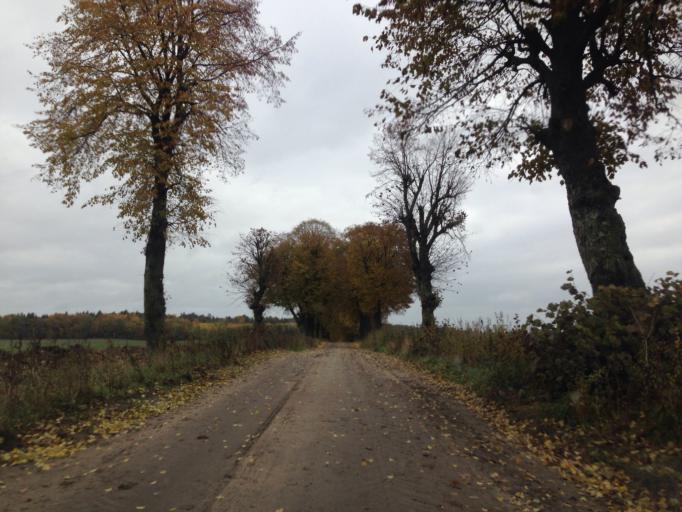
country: PL
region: Warmian-Masurian Voivodeship
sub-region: Powiat ilawski
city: Susz
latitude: 53.6746
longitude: 19.2887
